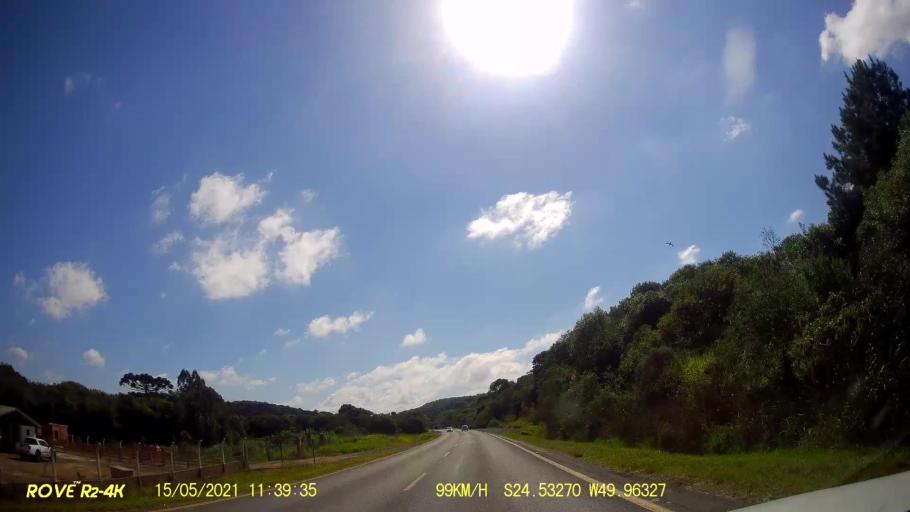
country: BR
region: Parana
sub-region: Pirai Do Sul
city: Pirai do Sul
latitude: -24.5328
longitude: -49.9633
